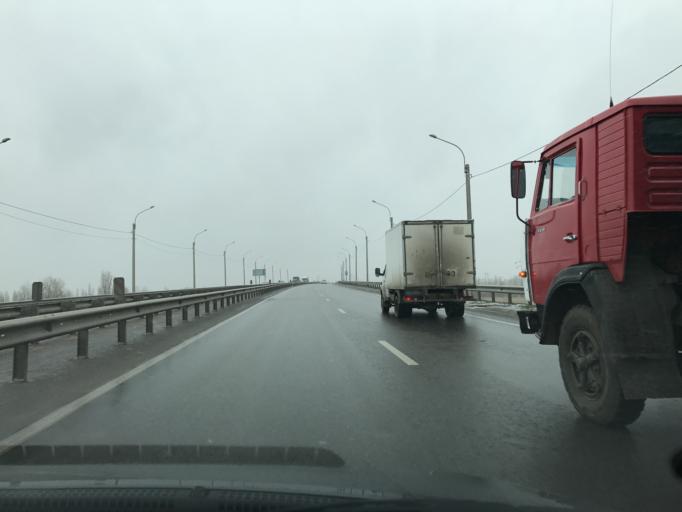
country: RU
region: Rostov
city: Bataysk
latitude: 47.1667
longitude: 39.7540
